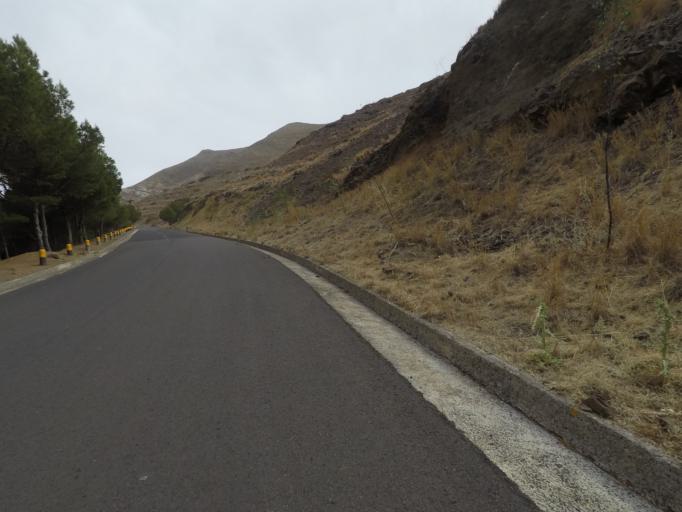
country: PT
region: Madeira
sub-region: Porto Santo
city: Camacha
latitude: 33.0902
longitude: -16.3105
